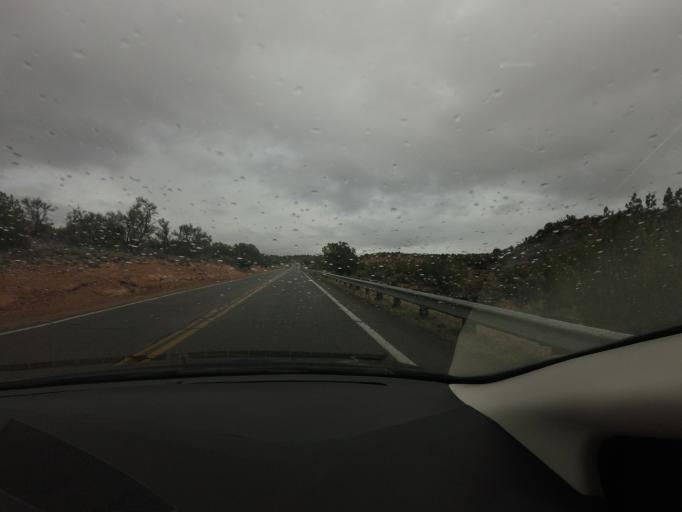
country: US
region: Arizona
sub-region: Yavapai County
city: Cornville
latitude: 34.7003
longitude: -111.8649
